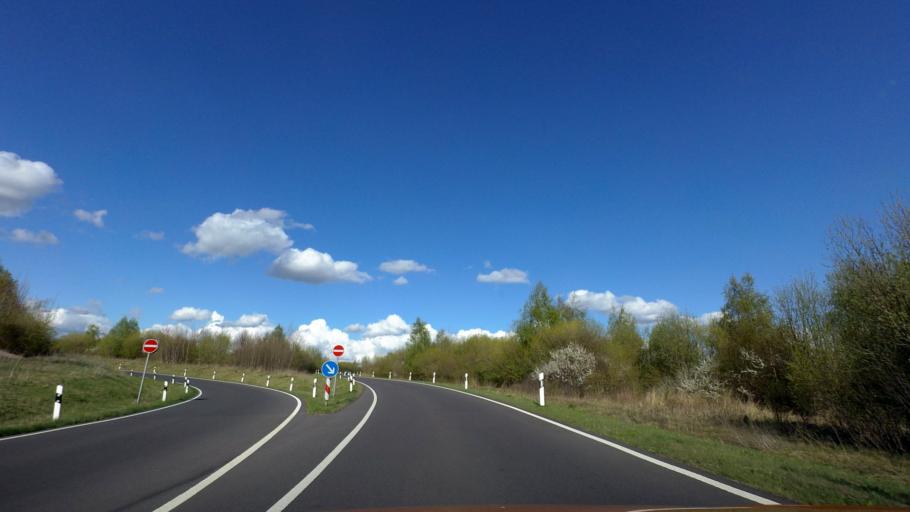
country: DE
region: Brandenburg
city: Pritzwalk
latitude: 53.1452
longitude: 12.1508
